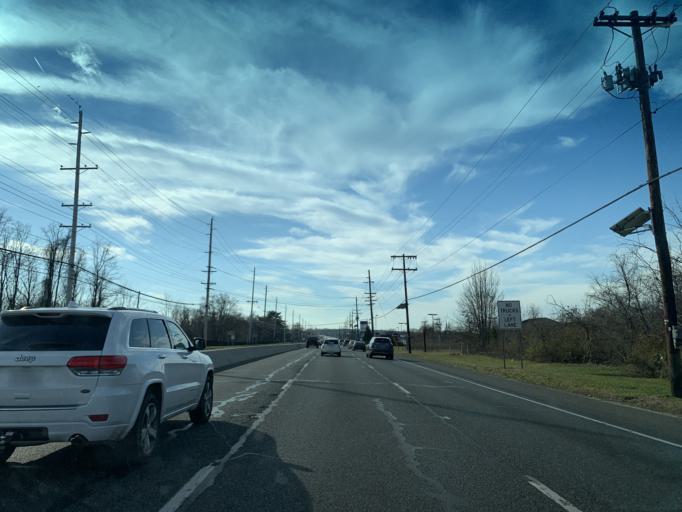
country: US
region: New Jersey
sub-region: Burlington County
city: Beverly
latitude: 40.0377
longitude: -74.9174
